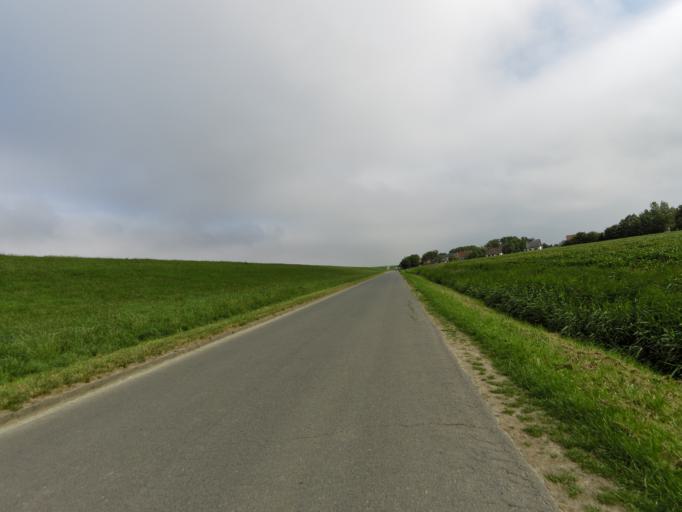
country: DE
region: Lower Saxony
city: Padingbuttel
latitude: 53.7515
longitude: 8.5308
